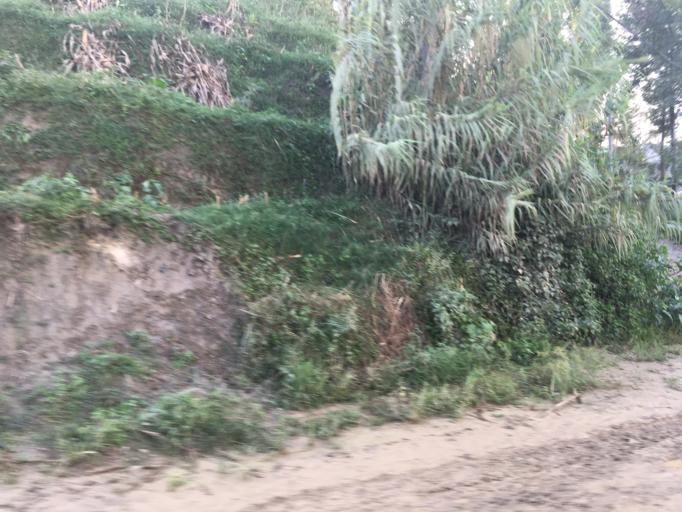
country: NP
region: Central Region
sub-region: Bagmati Zone
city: Bhaktapur
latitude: 27.6938
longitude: 85.4614
